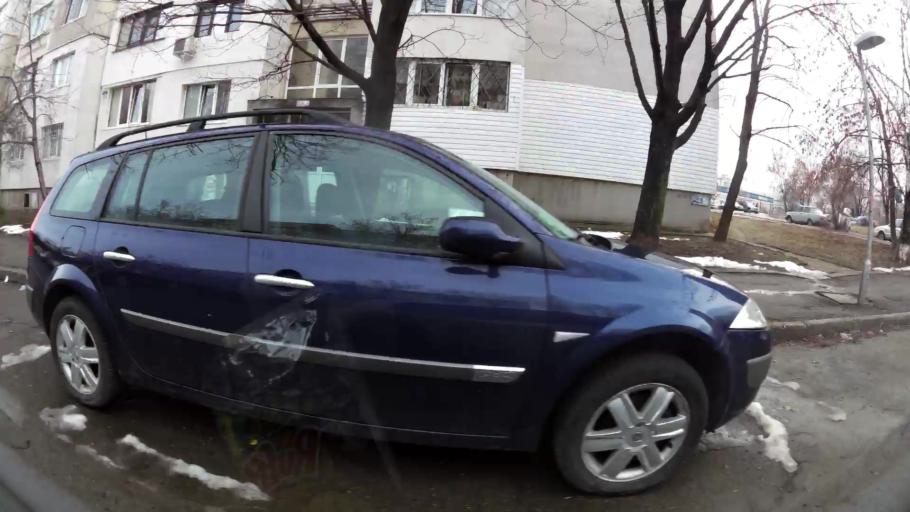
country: BG
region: Sofiya
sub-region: Obshtina Bozhurishte
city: Bozhurishte
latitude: 42.7144
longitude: 23.2476
